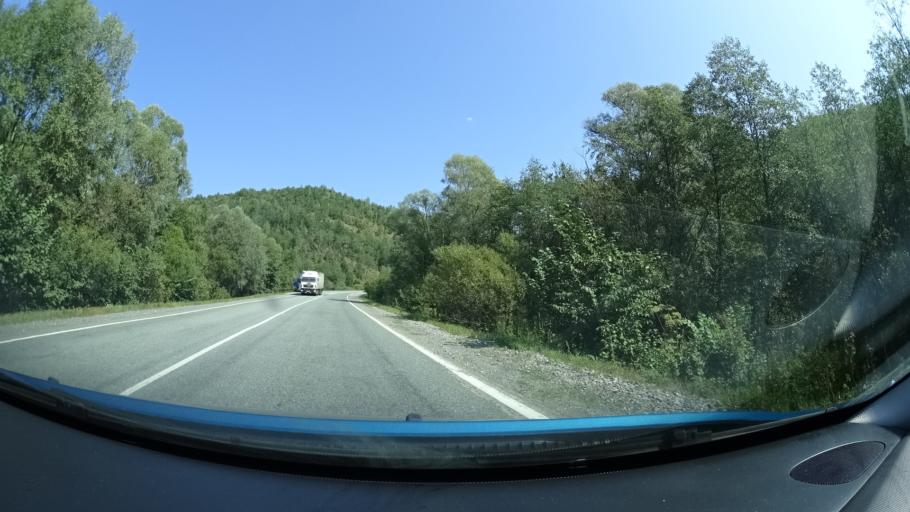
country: RU
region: Bashkortostan
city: Inzer
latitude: 54.3125
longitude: 57.1964
